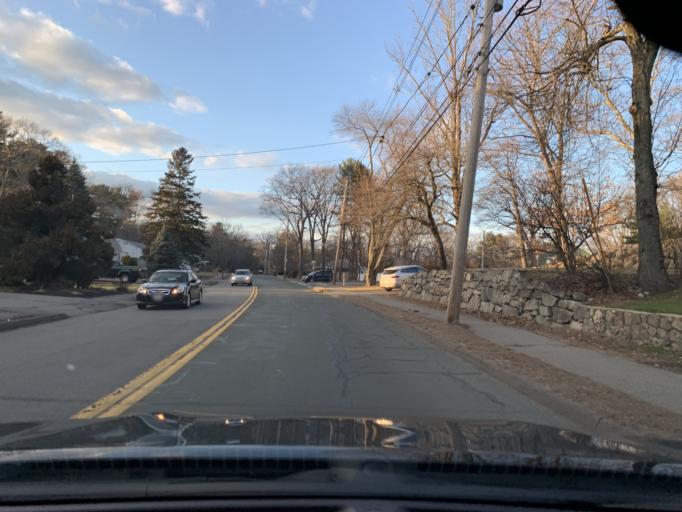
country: US
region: Massachusetts
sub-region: Essex County
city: Lynnfield
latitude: 42.5201
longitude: -71.0164
